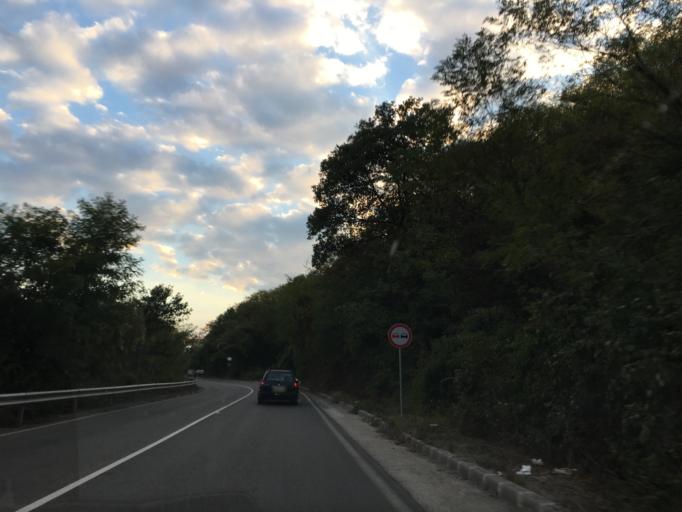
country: BG
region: Sofiya
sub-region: Obshtina Svoge
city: Svoge
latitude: 42.8456
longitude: 23.3706
